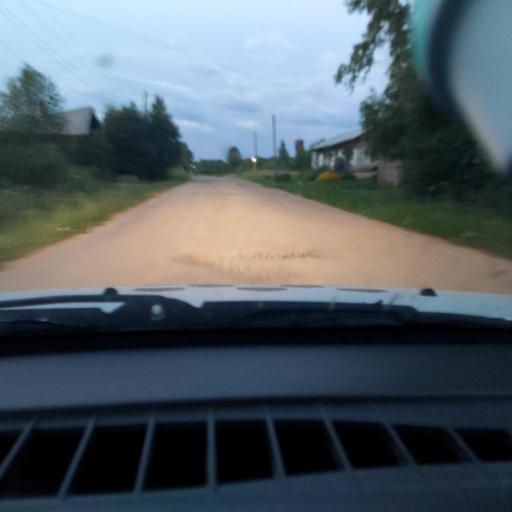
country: RU
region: Kirov
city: Darovskoy
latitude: 58.9891
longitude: 47.8737
